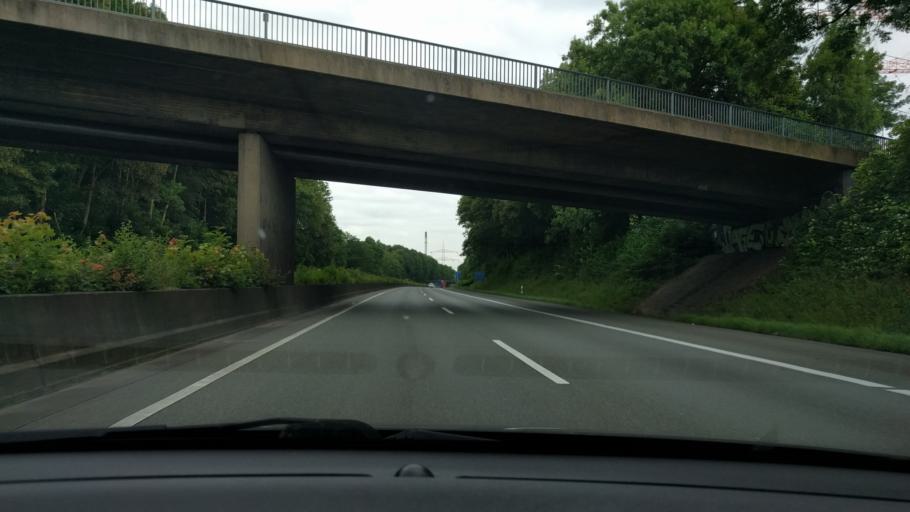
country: DE
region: North Rhine-Westphalia
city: Castrop-Rauxel
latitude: 51.5466
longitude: 7.3600
